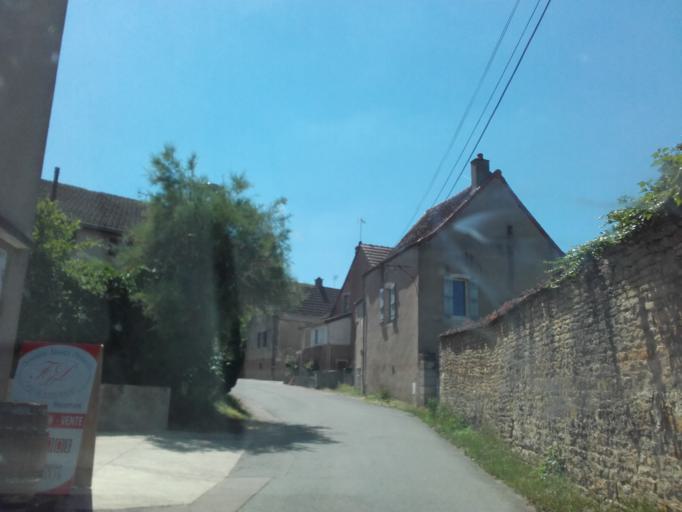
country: FR
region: Bourgogne
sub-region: Departement de Saone-et-Loire
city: Saint-Leger-sur-Dheune
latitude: 46.8960
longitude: 4.6674
